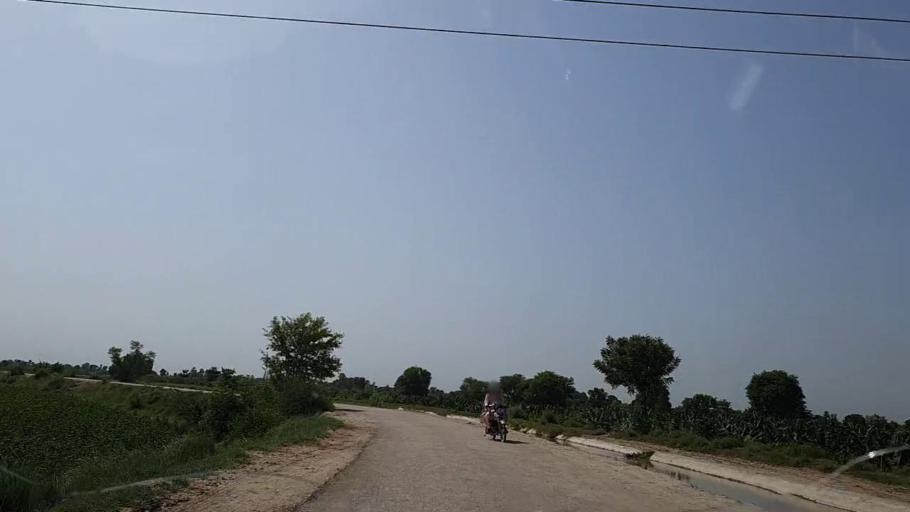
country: PK
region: Sindh
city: Kandiaro
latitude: 27.0501
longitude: 68.1627
